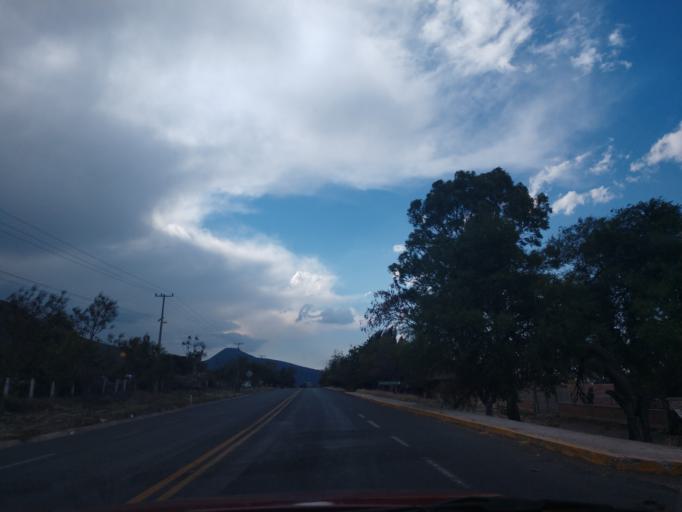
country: MX
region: Jalisco
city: Jocotepec
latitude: 20.2249
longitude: -103.4122
